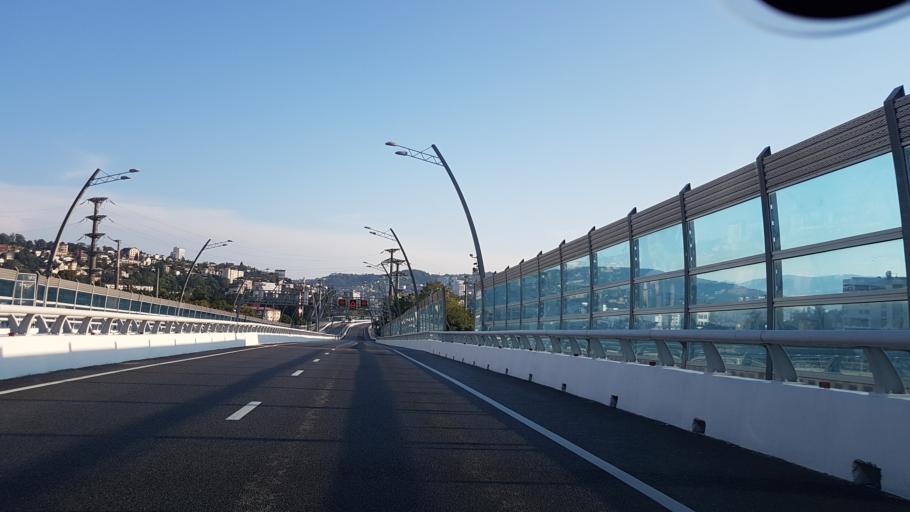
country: RU
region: Krasnodarskiy
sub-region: Sochi City
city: Sochi
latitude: 43.5971
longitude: 39.7315
